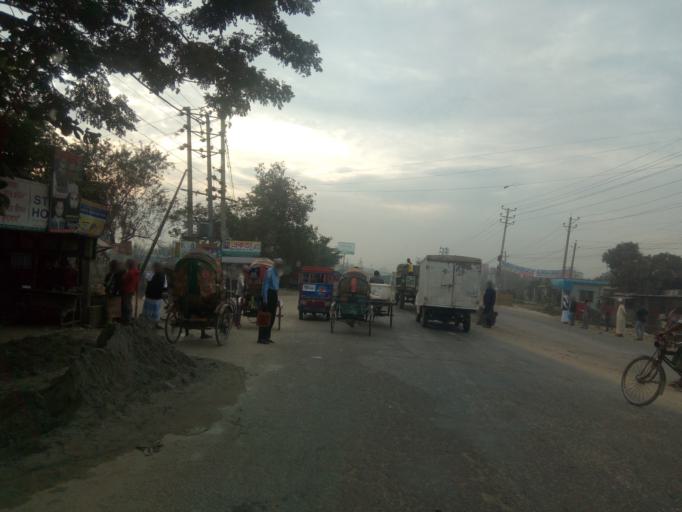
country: BD
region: Dhaka
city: Narayanganj
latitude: 23.6512
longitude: 90.4914
